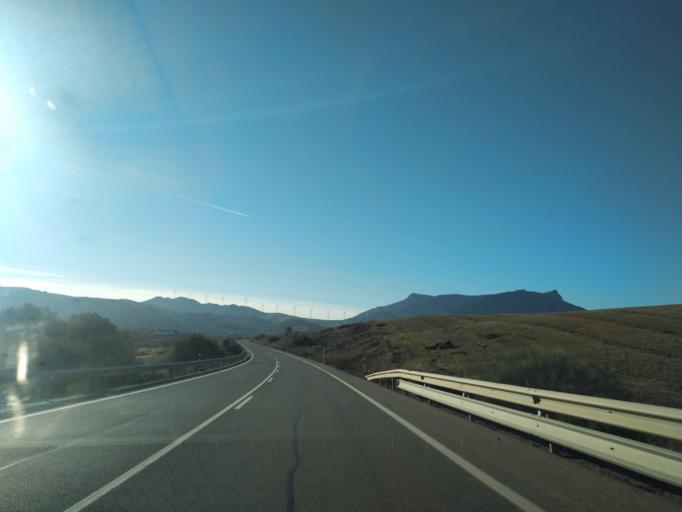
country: ES
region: Andalusia
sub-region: Provincia de Malaga
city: Ardales
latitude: 36.9087
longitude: -4.8420
